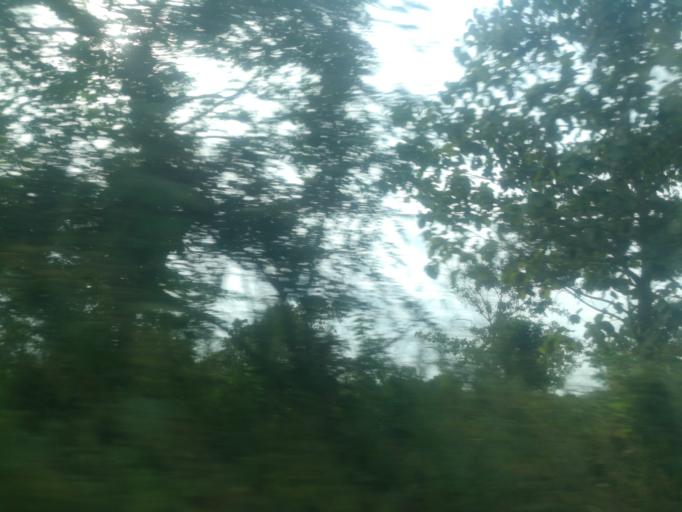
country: NG
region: Ogun
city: Ayetoro
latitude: 7.3239
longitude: 3.0684
